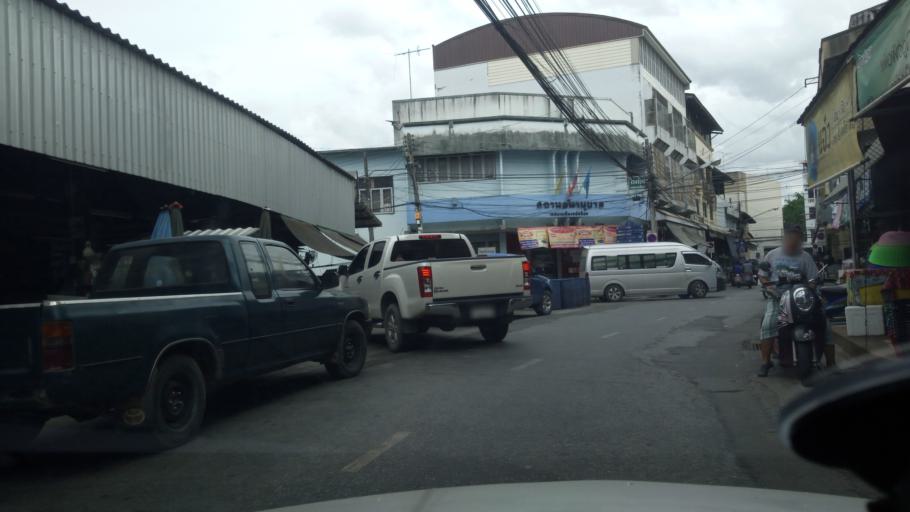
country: TH
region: Chon Buri
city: Phanat Nikhom
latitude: 13.4536
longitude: 101.1815
